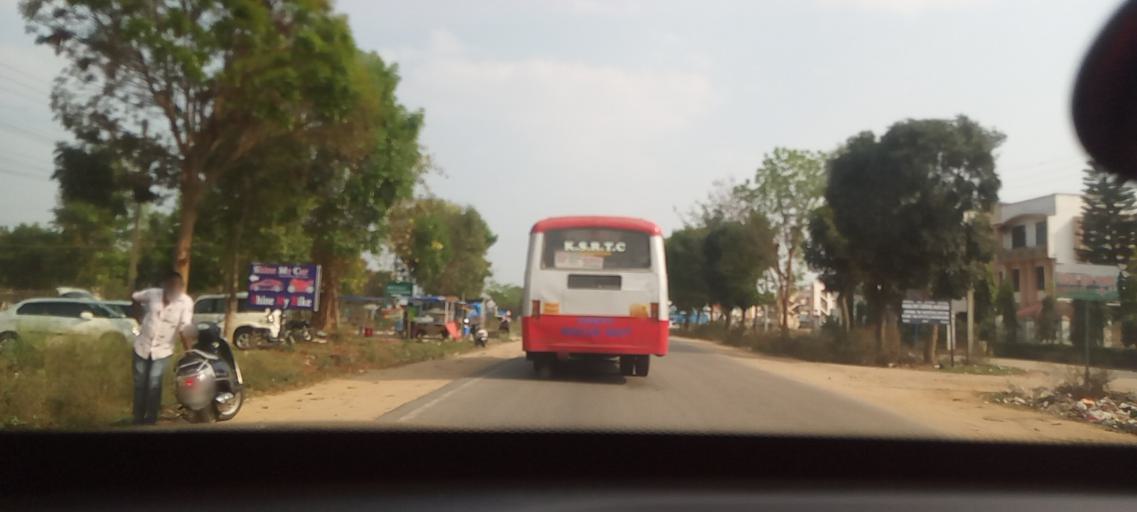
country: IN
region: Karnataka
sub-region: Hassan
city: Hassan
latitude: 13.0023
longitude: 76.0742
